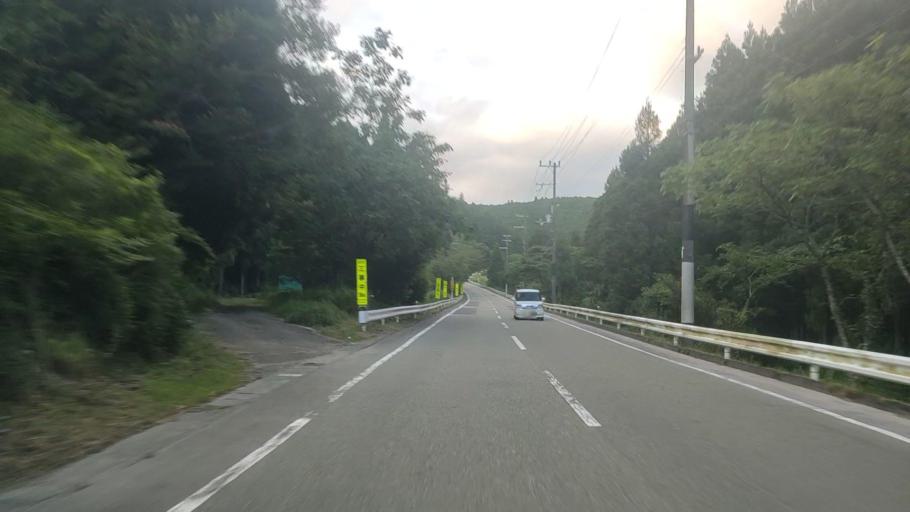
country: JP
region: Wakayama
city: Tanabe
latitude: 33.8298
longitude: 135.6431
